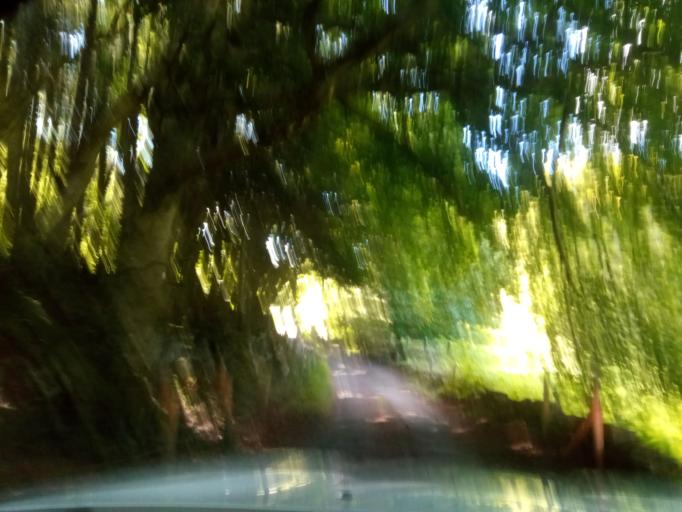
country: GB
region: Scotland
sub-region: Argyll and Bute
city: Isle Of Mull
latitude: 56.7805
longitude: -5.8257
